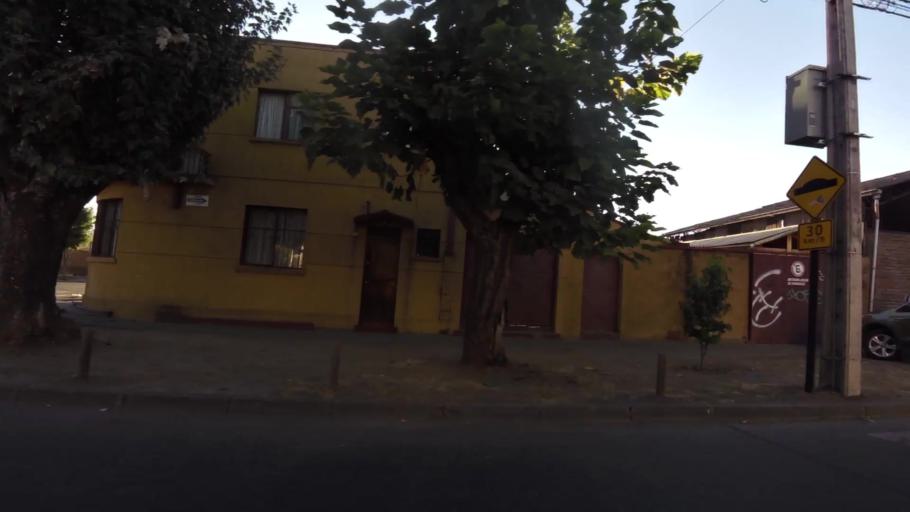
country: CL
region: Maule
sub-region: Provincia de Curico
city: Curico
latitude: -34.9784
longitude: -71.2435
